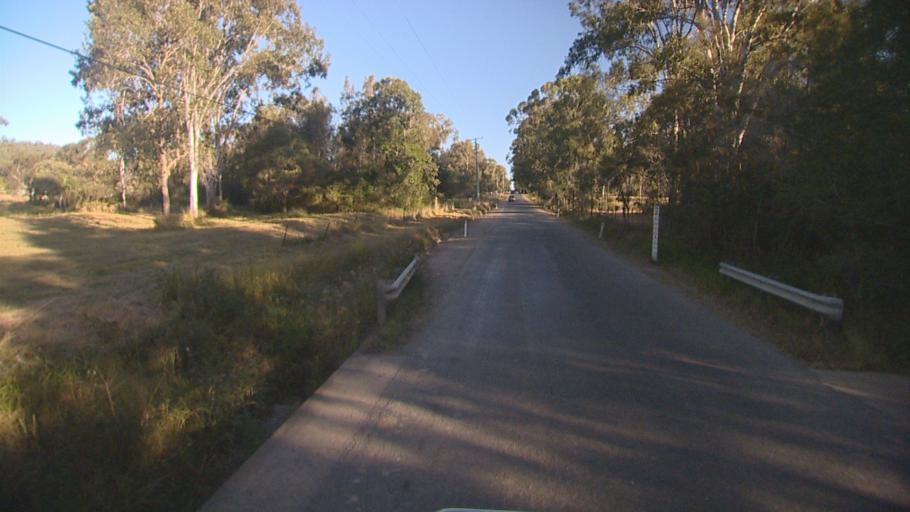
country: AU
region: Queensland
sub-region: Logan
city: Logan Reserve
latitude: -27.7586
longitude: 153.1398
